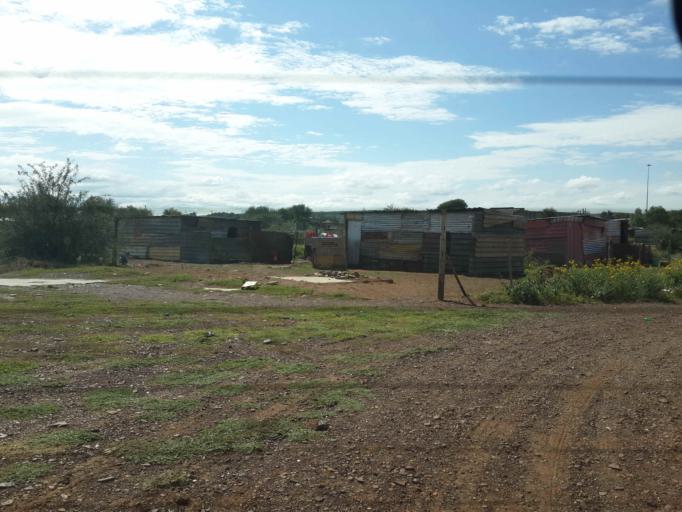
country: ZA
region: Northern Cape
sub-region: Siyanda District Municipality
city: Danielskuil
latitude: -28.1939
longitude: 23.5437
